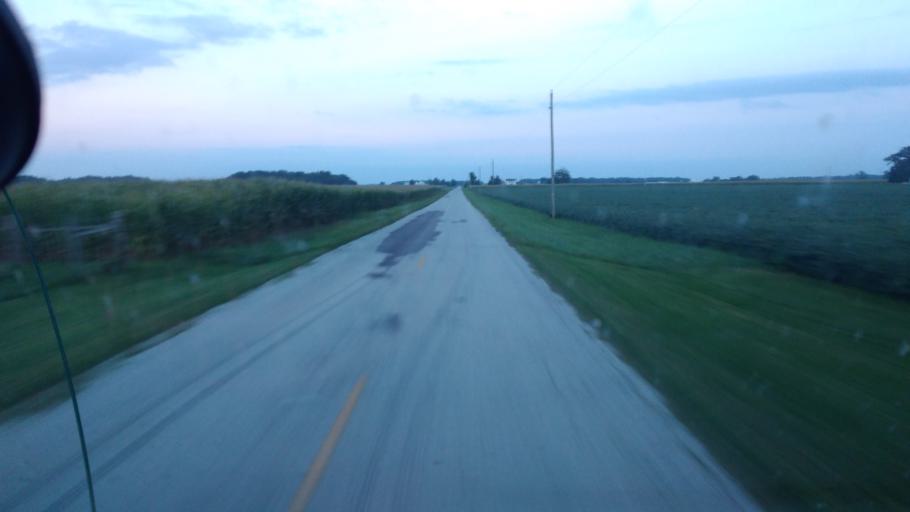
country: US
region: Ohio
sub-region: Hardin County
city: Forest
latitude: 40.6727
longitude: -83.4642
